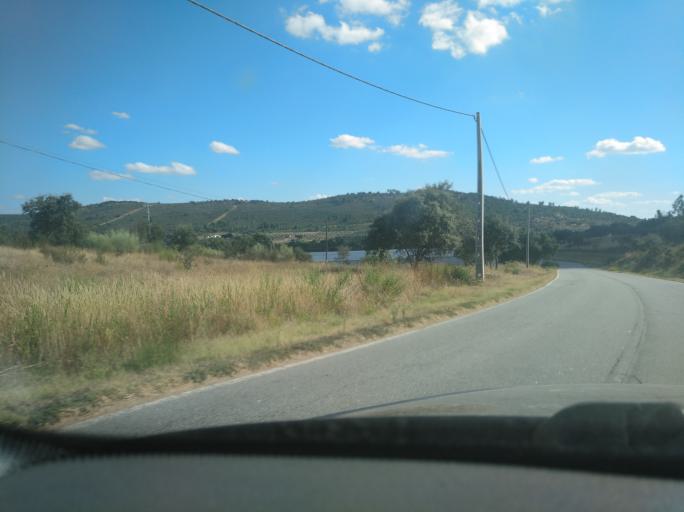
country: ES
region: Extremadura
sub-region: Provincia de Badajoz
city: La Codosera
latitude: 39.1653
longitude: -7.1854
